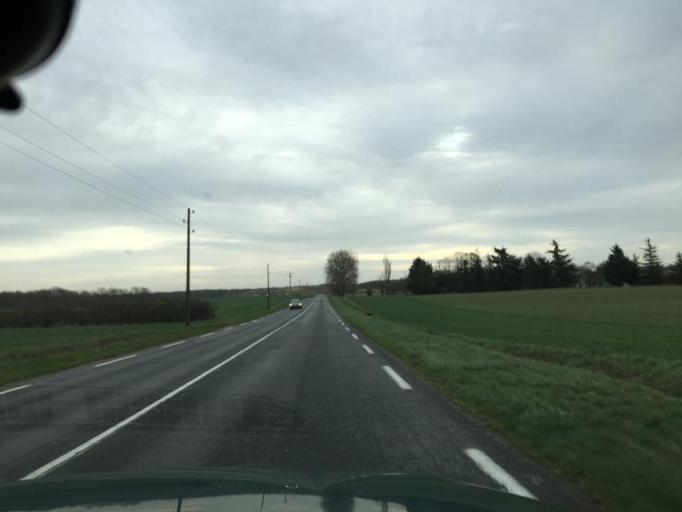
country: FR
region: Centre
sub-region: Departement du Loiret
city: Huisseau-sur-Mauves
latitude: 47.9270
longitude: 1.7136
